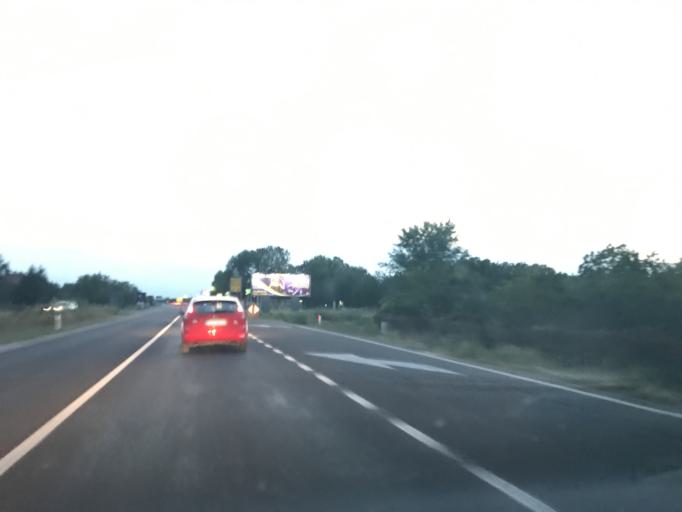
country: RS
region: Central Serbia
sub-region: Branicevski Okrug
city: Pozarevac
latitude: 44.6032
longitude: 21.1321
